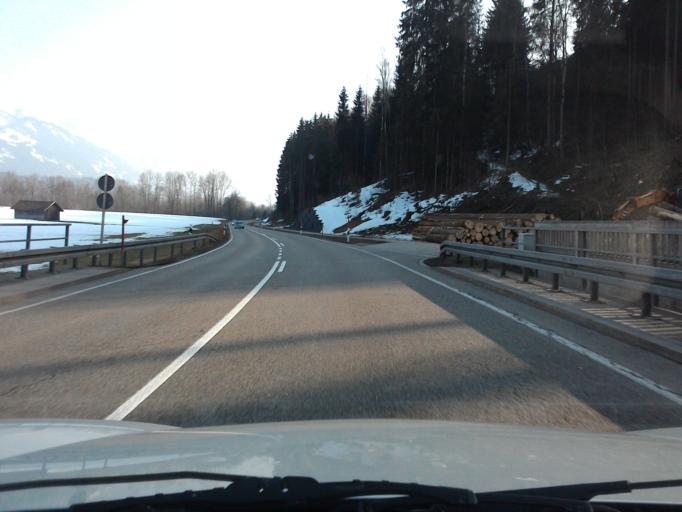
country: DE
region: Bavaria
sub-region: Swabia
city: Sonthofen
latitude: 47.4961
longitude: 10.2654
